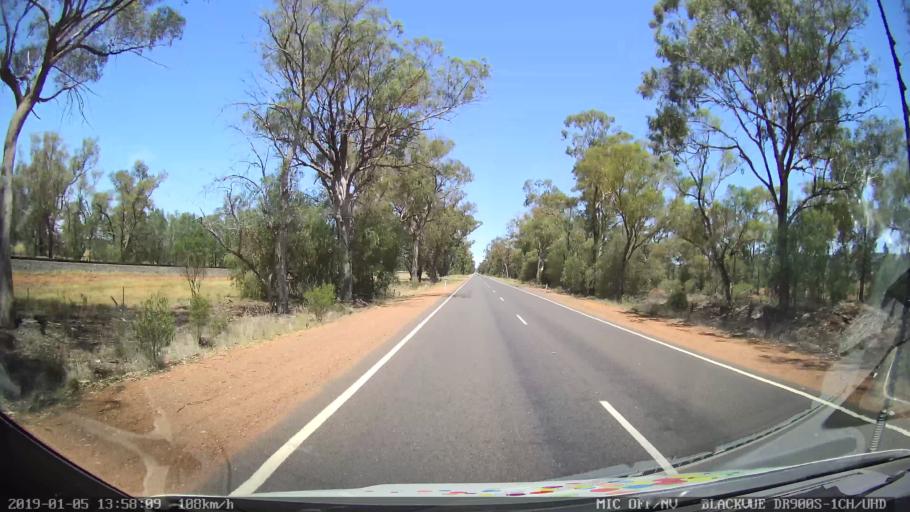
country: AU
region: New South Wales
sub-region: Gunnedah
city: Gunnedah
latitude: -31.1358
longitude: 150.2816
